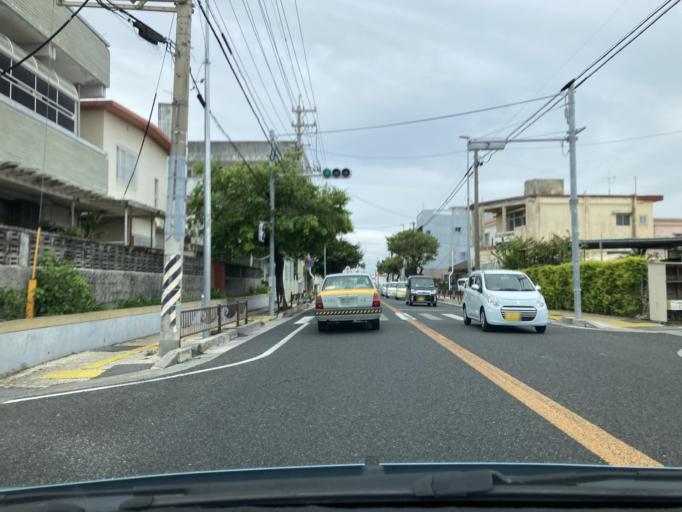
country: JP
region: Okinawa
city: Itoman
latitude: 26.1318
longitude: 127.6700
